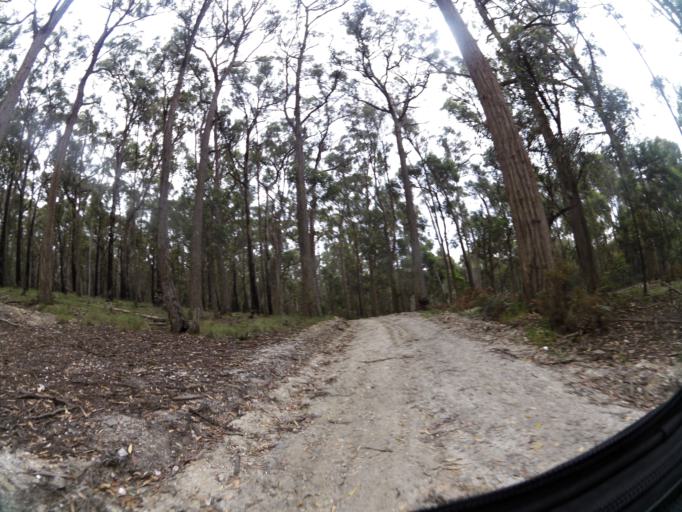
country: AU
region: Victoria
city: Brown Hill
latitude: -37.5124
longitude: 143.9147
